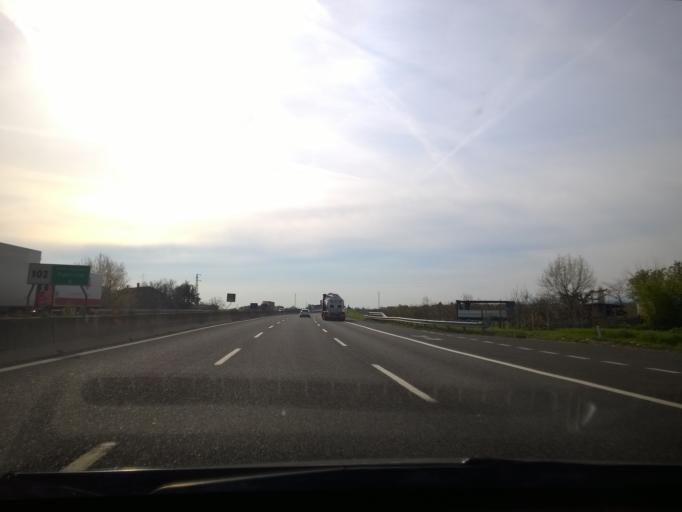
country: IT
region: Emilia-Romagna
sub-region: Forli-Cesena
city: Bagnarola
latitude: 44.1579
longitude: 12.3113
